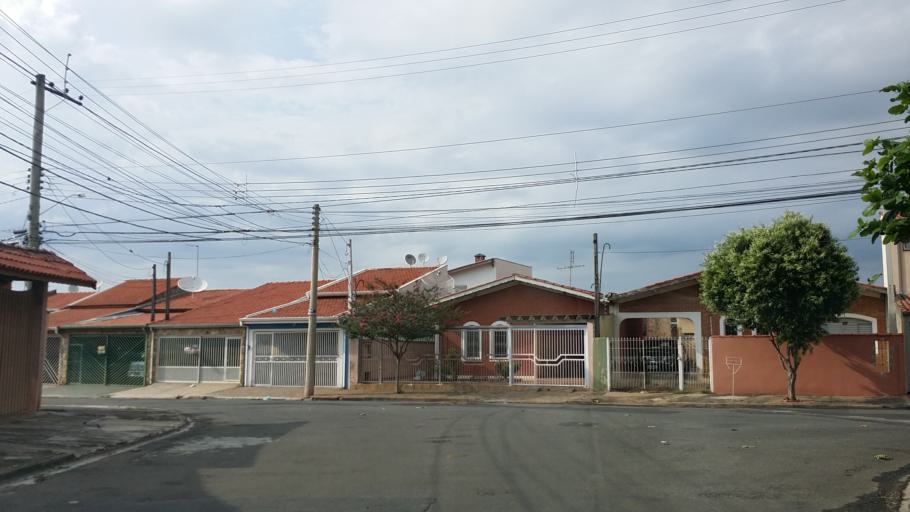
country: BR
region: Sao Paulo
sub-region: Indaiatuba
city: Indaiatuba
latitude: -23.1034
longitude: -47.2090
